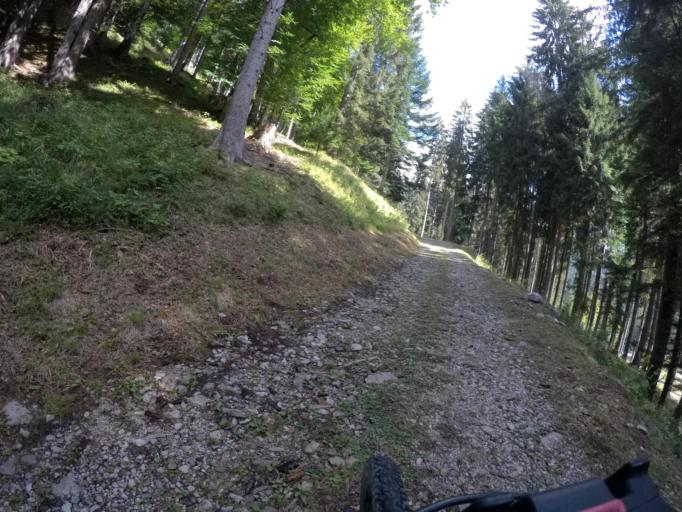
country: IT
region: Friuli Venezia Giulia
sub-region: Provincia di Udine
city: Paularo
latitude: 46.5063
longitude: 13.1798
